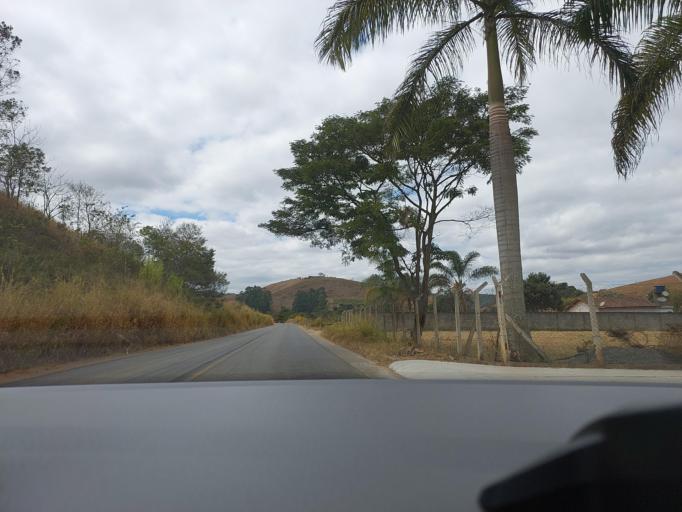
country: BR
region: Minas Gerais
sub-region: Vicosa
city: Vicosa
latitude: -20.8273
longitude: -42.7417
